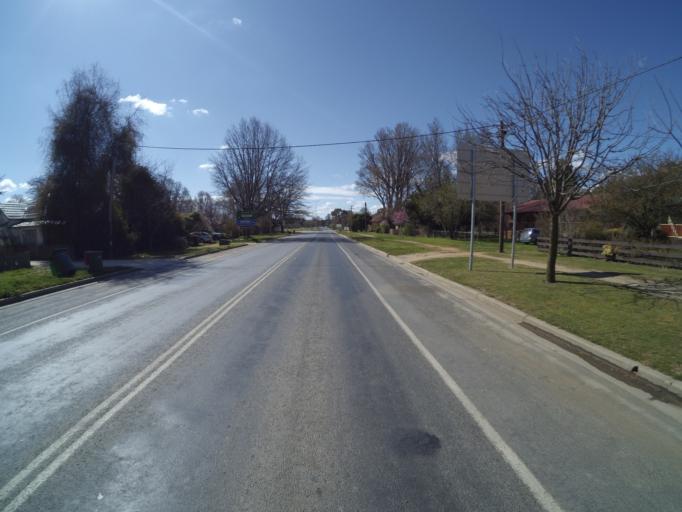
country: AU
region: New South Wales
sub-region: Palerang
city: Bungendore
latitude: -35.2550
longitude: 149.4381
